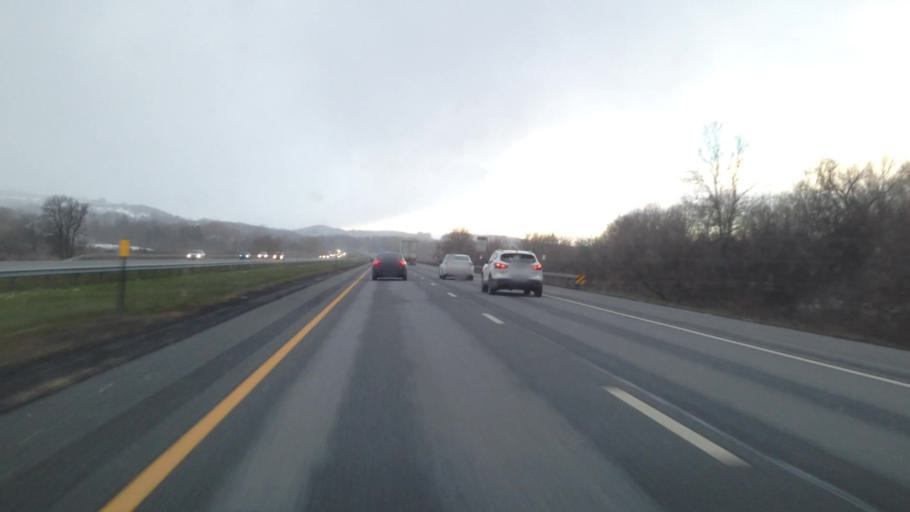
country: US
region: New York
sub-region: Montgomery County
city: Saint Johnsville
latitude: 43.0026
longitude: -74.7624
